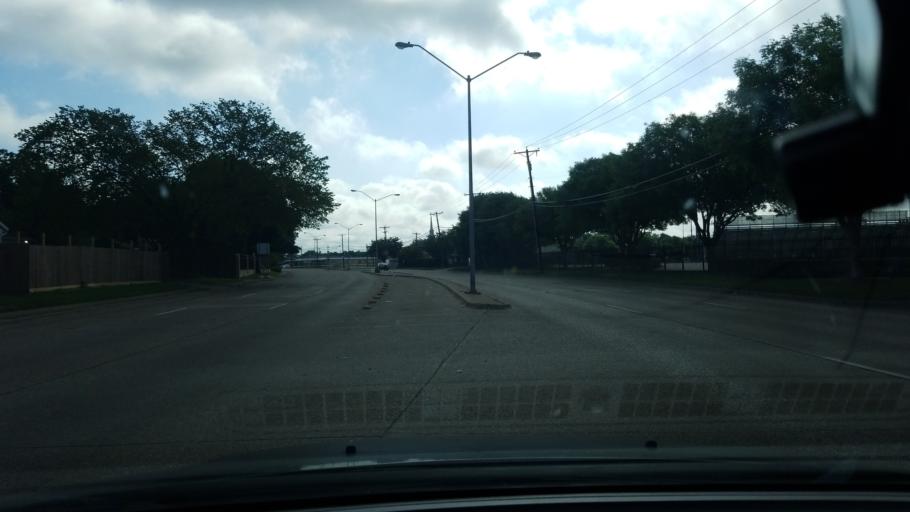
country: US
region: Texas
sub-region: Dallas County
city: Mesquite
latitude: 32.8194
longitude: -96.6818
